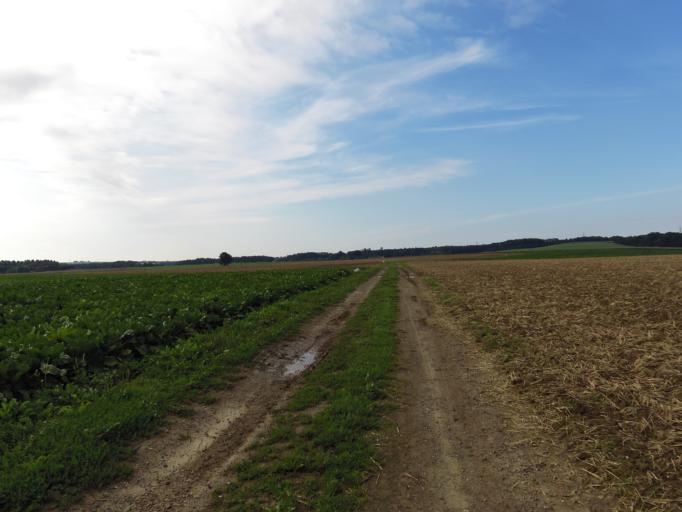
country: NL
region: Limburg
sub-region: Gemeente Voerendaal
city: Klimmen
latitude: 50.8935
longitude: 5.8925
